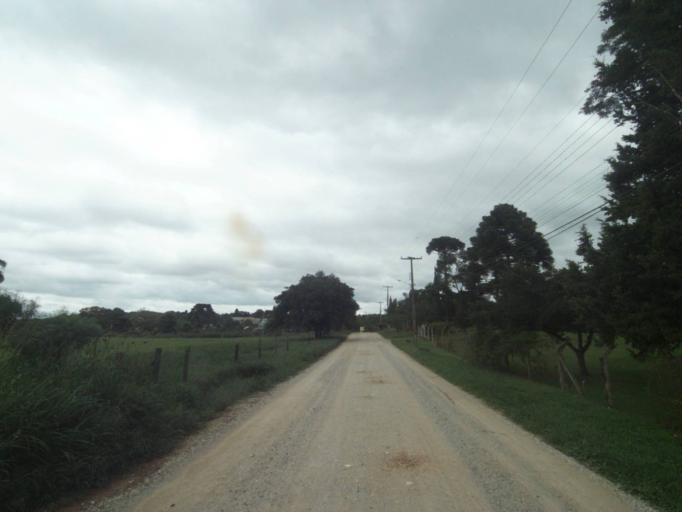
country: BR
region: Parana
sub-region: Quatro Barras
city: Quatro Barras
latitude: -25.3269
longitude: -49.0910
